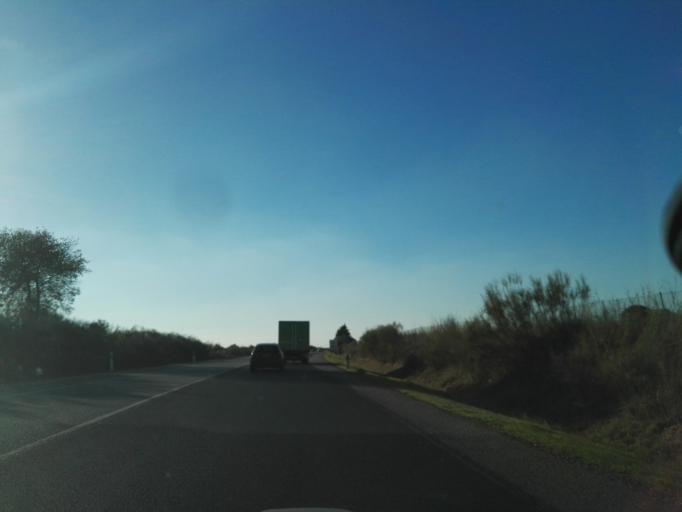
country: PT
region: Evora
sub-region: Borba
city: Borba
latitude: 38.8244
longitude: -7.5152
